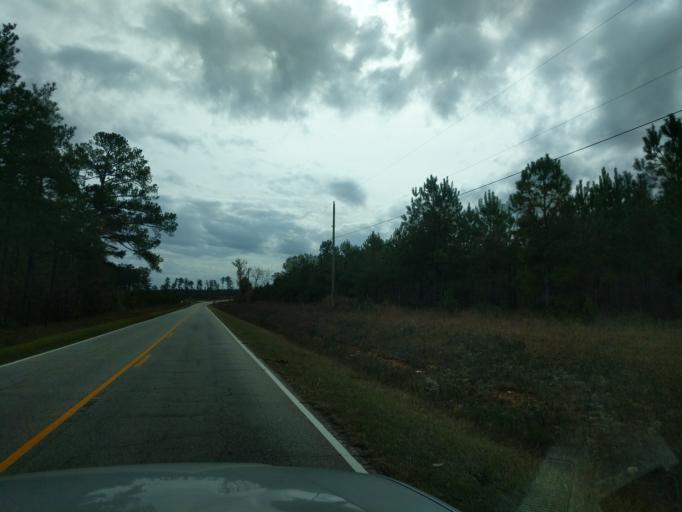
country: US
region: South Carolina
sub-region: Saluda County
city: Saluda
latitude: 34.1153
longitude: -81.8335
